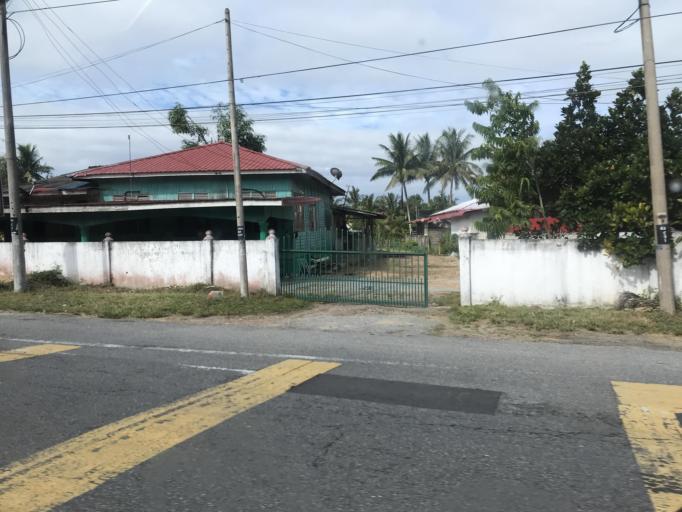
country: MY
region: Kelantan
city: Kota Bharu
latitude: 6.1282
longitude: 102.1796
